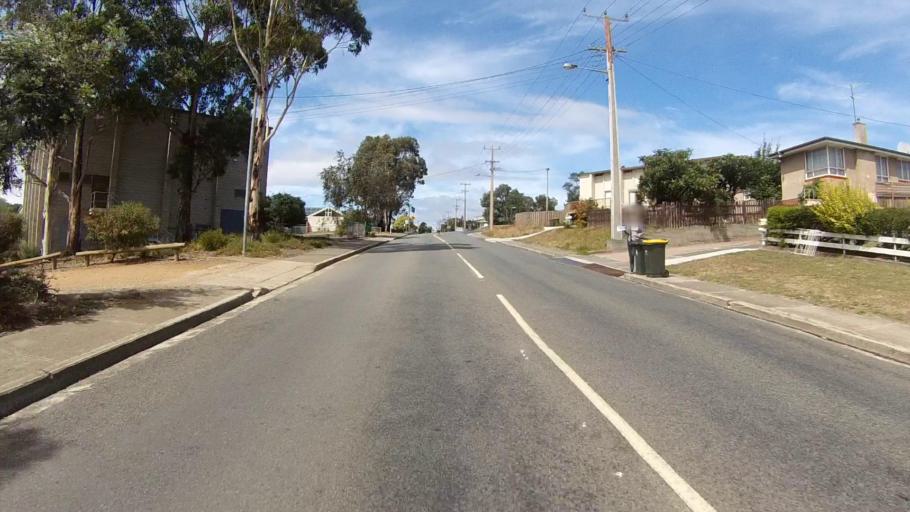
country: AU
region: Tasmania
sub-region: Clarence
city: Lindisfarne
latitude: -42.8111
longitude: 147.3512
